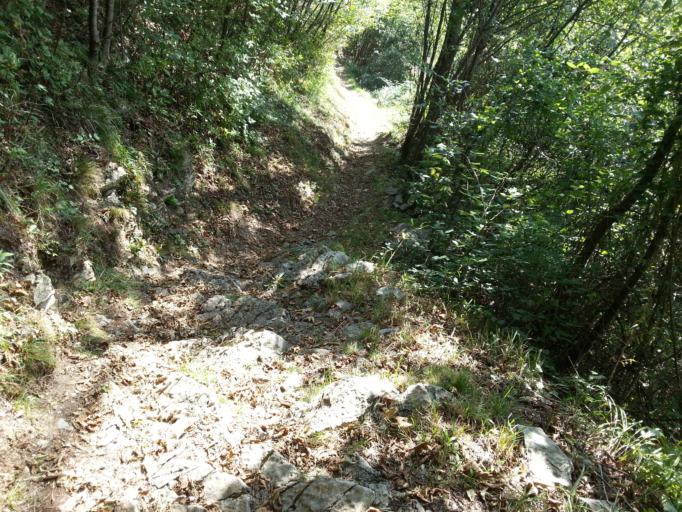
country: IT
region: Lombardy
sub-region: Provincia di Lecco
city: Pasturo
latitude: 45.9389
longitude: 9.4341
